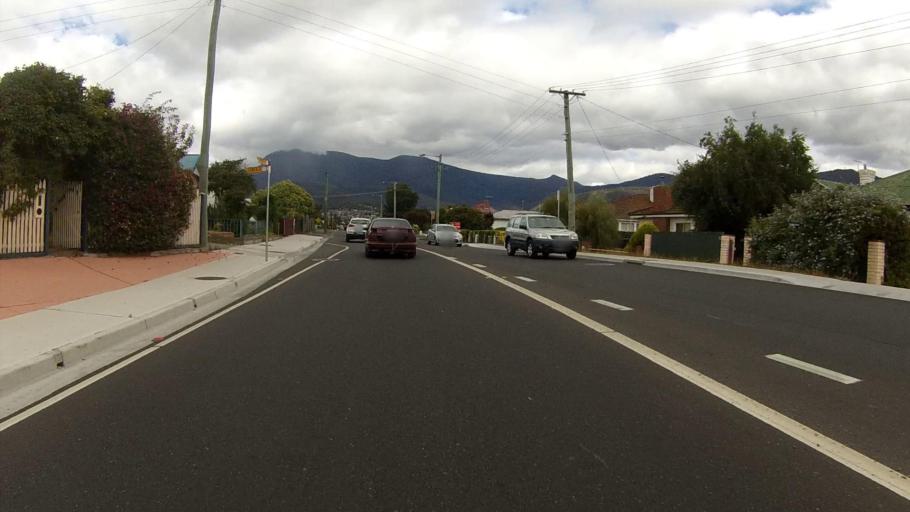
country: AU
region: Tasmania
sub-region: Glenorchy
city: Glenorchy
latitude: -42.8287
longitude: 147.2835
